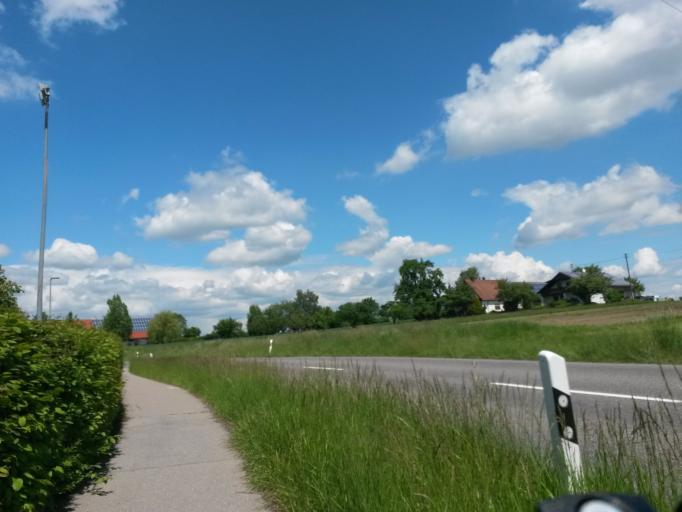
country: DE
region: Baden-Wuerttemberg
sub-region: Tuebingen Region
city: Bad Schussenried
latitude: 47.9781
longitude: 9.6778
